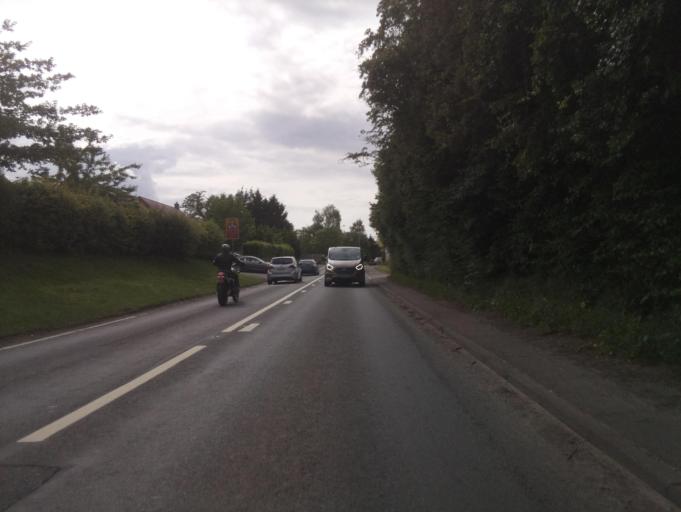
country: GB
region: England
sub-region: Worcestershire
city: Bransford
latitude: 52.1716
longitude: -2.2968
